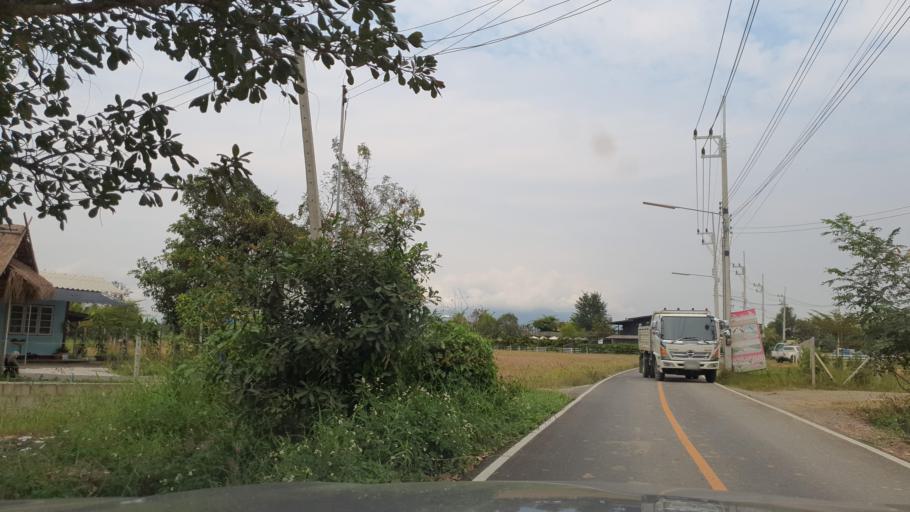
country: TH
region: Chiang Mai
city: Hang Dong
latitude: 18.6792
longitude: 98.9601
